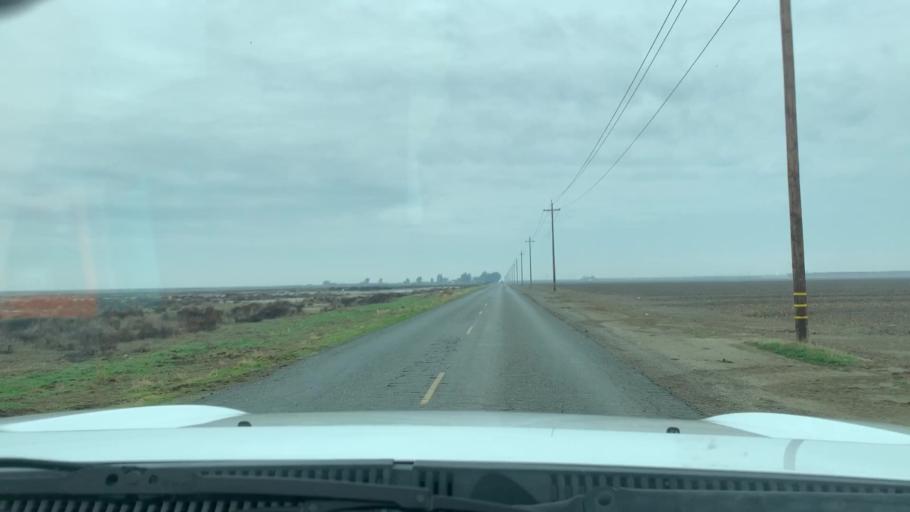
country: US
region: California
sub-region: Tulare County
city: Alpaugh
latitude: 35.7610
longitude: -119.4322
